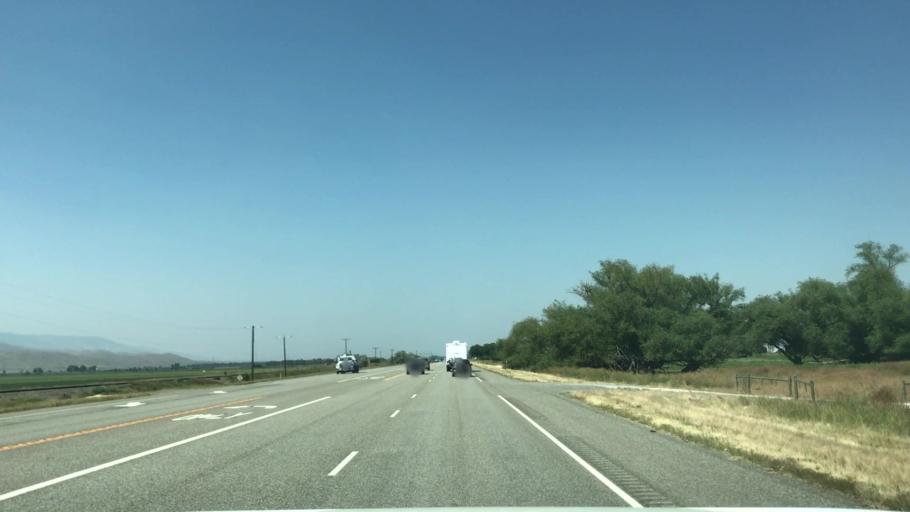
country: US
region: Montana
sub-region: Broadwater County
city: Townsend
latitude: 46.2097
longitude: -111.4562
